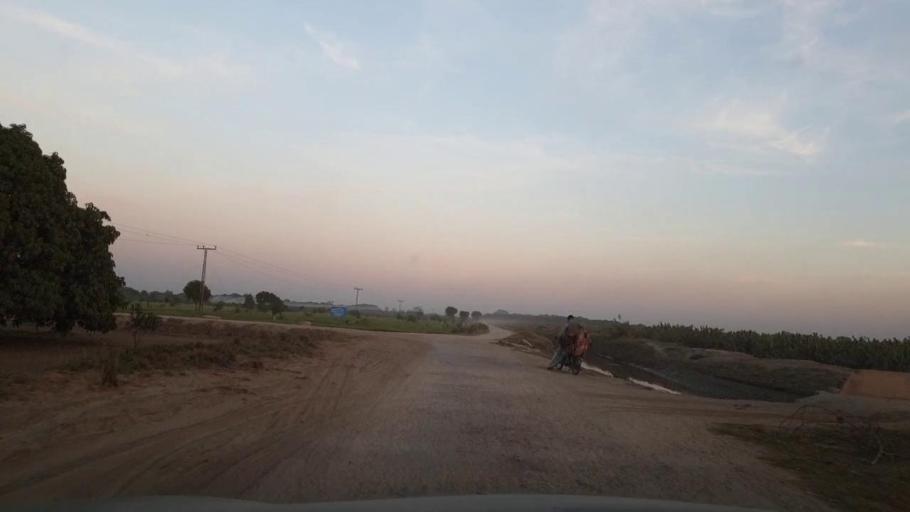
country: PK
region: Sindh
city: Tando Allahyar
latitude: 25.5641
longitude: 68.7635
